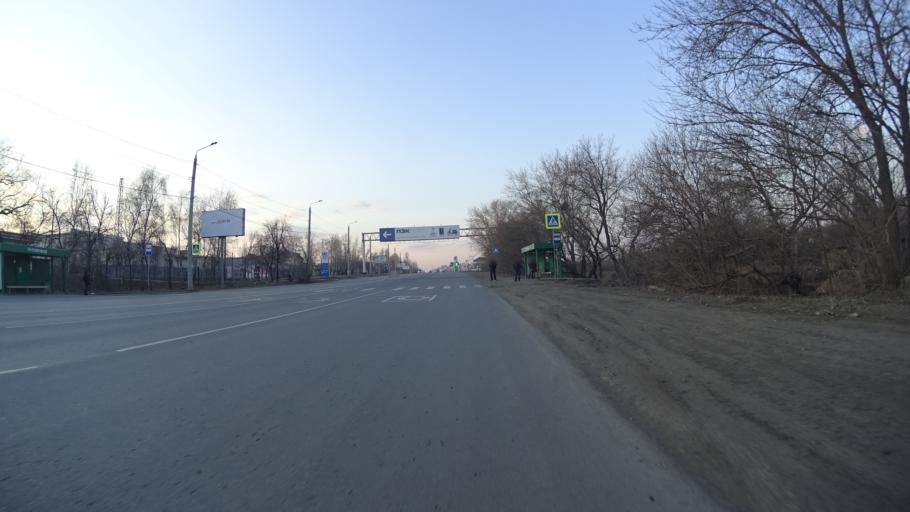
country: RU
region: Chelyabinsk
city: Novosineglazovskiy
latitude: 55.0858
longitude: 61.3884
